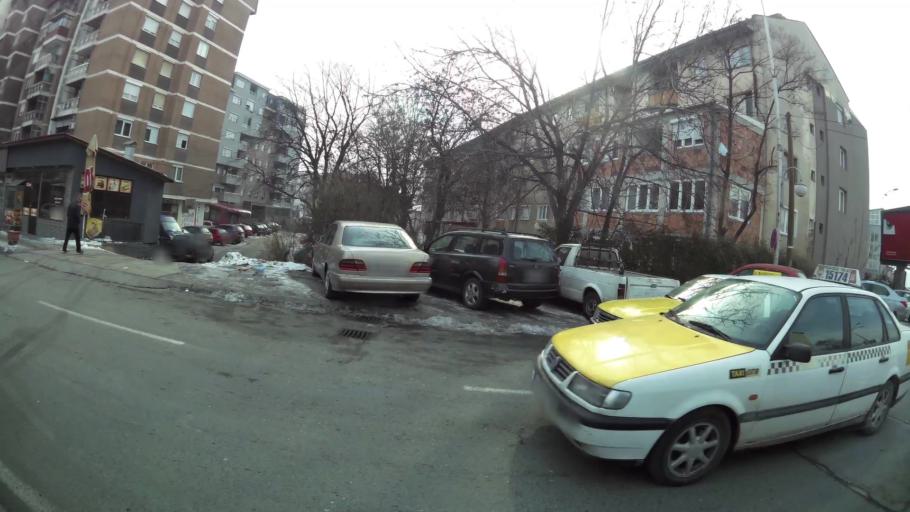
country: MK
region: Cair
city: Cair
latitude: 42.0129
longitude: 21.4324
